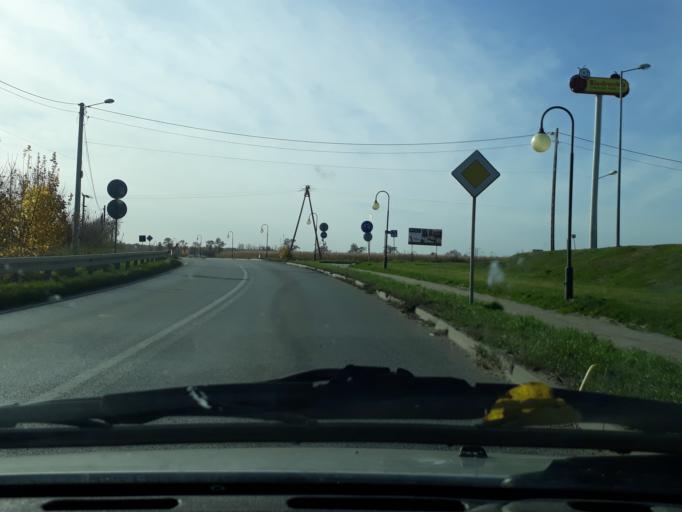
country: PL
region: Silesian Voivodeship
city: Wozniki
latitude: 50.5886
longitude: 19.0556
